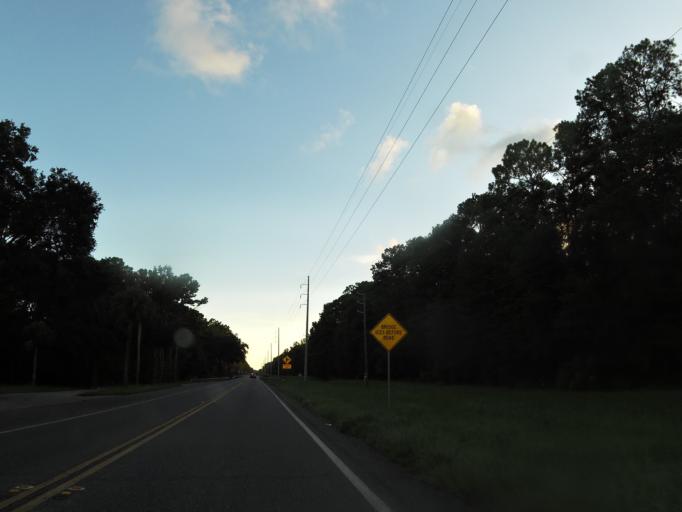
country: US
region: Georgia
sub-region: Glynn County
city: Dock Junction
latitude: 31.1346
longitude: -81.5977
